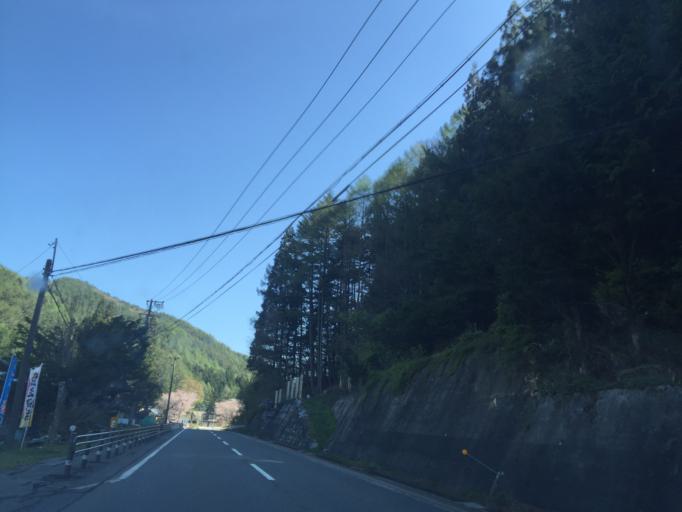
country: JP
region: Nagano
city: Iida
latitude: 35.3893
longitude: 137.6833
